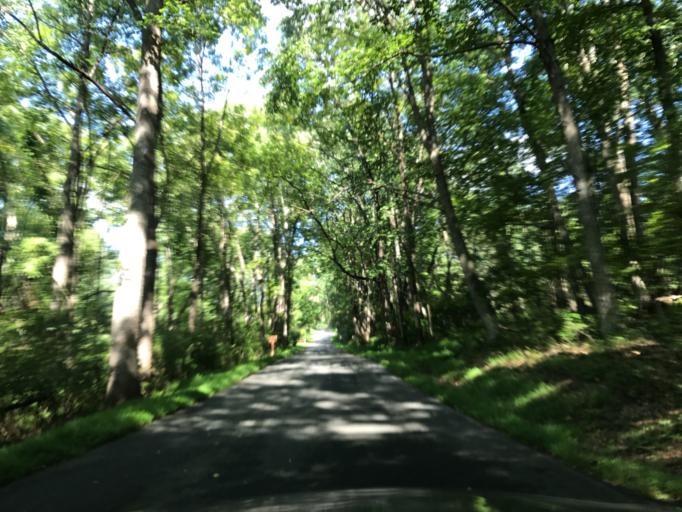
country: US
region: Pennsylvania
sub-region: York County
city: New Freedom
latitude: 39.6229
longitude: -76.6849
